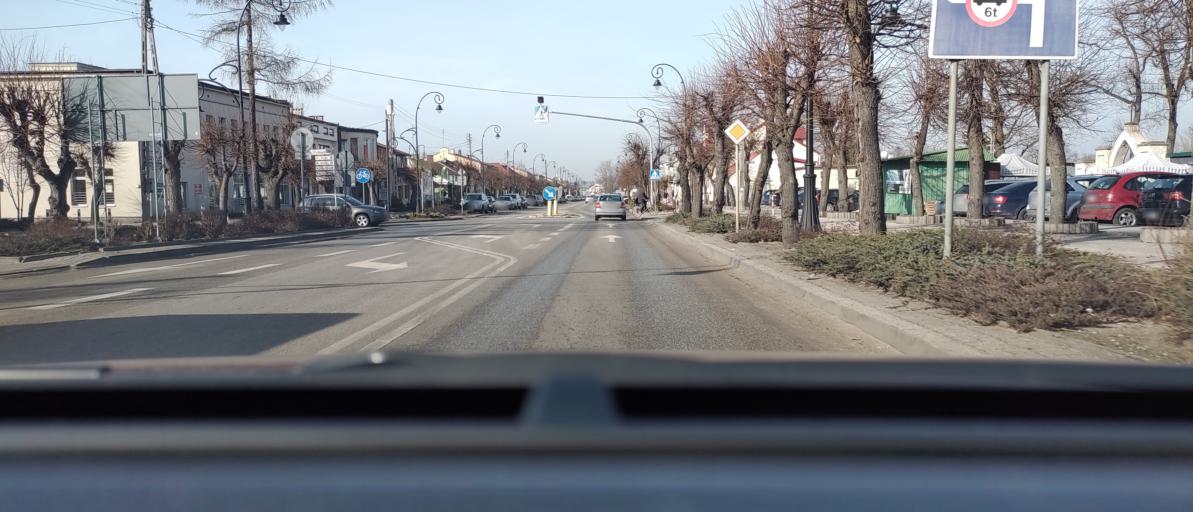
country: PL
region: Masovian Voivodeship
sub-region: Powiat bialobrzeski
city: Bialobrzegi
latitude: 51.6466
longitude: 20.9565
